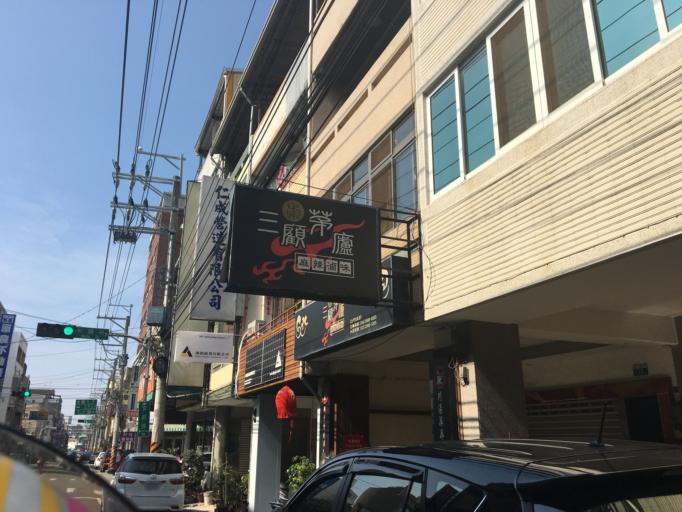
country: TW
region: Taiwan
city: Fengyuan
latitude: 24.3480
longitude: 120.6208
